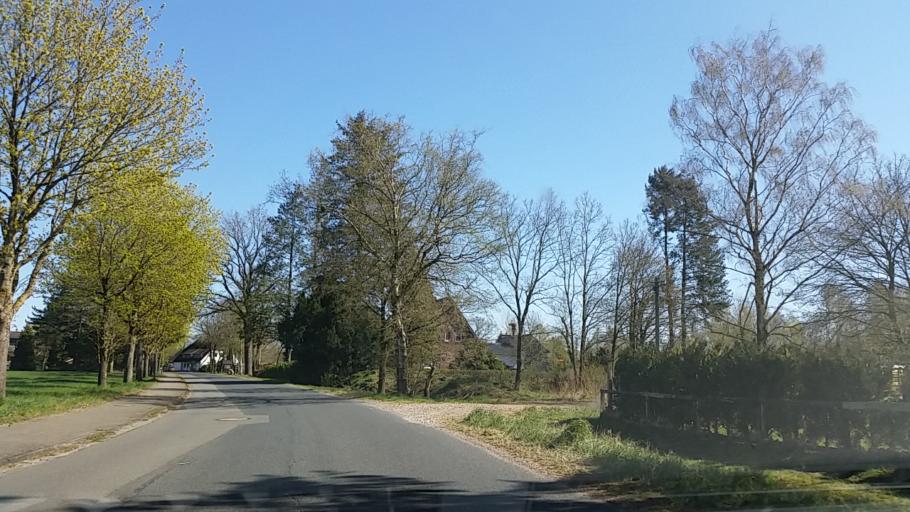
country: DE
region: Lower Saxony
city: Handeloh
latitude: 53.1857
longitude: 9.8298
